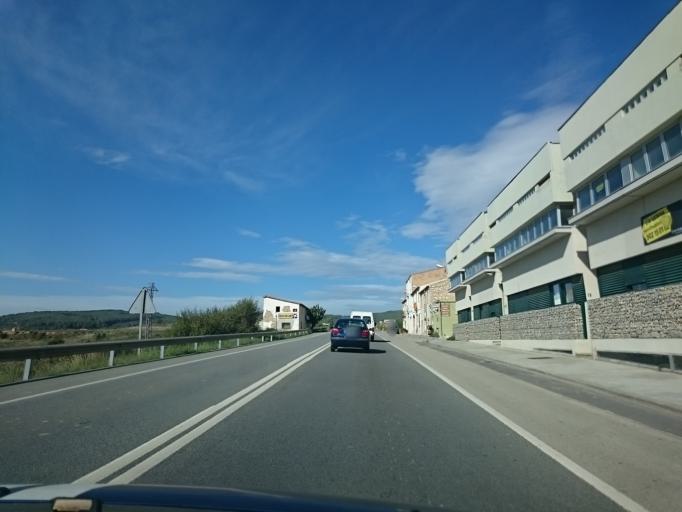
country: ES
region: Catalonia
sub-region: Provincia de Barcelona
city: Avinyonet del Penedes
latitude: 41.3707
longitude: 1.8040
